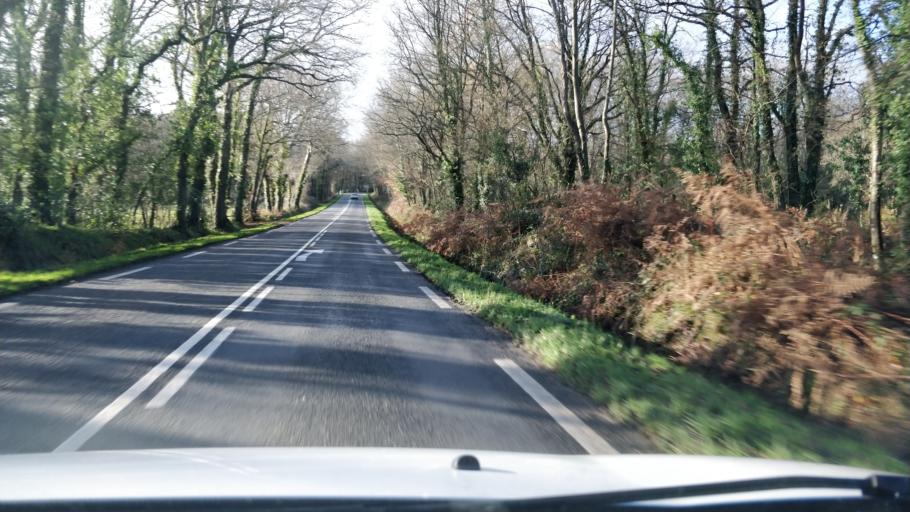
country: FR
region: Pays de la Loire
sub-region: Departement de la Loire-Atlantique
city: Herbignac
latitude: 47.4388
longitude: -2.3384
